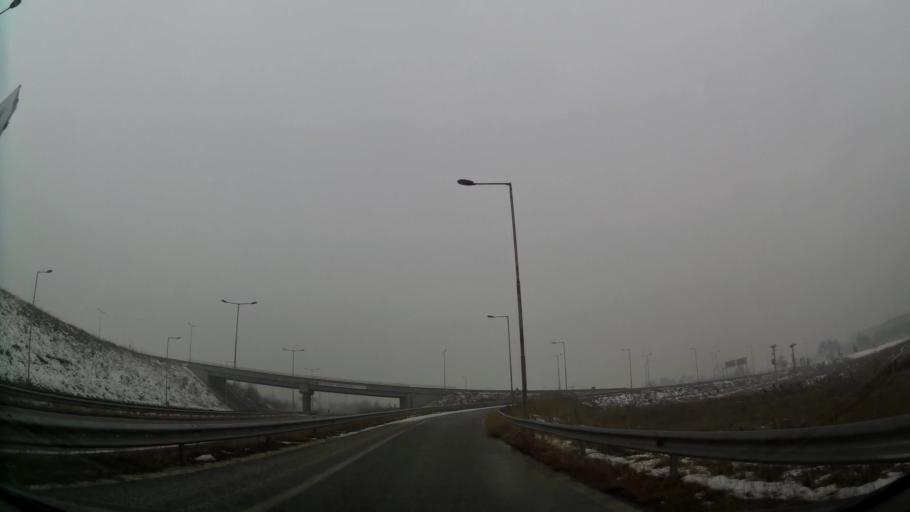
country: MK
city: Miladinovci
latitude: 41.9599
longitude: 21.6325
